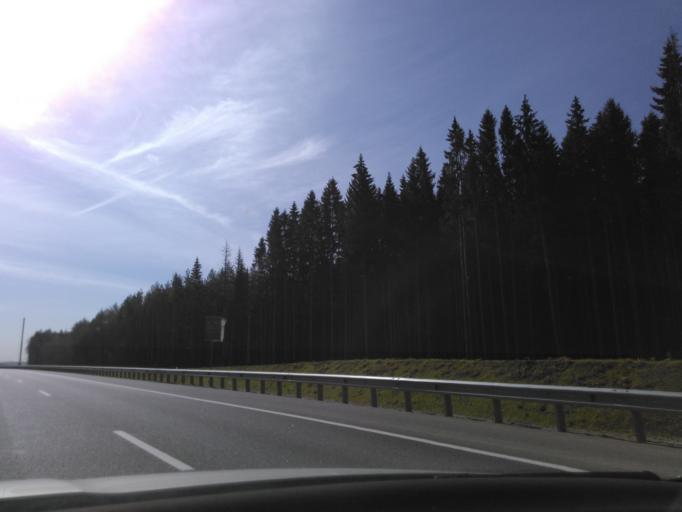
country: RU
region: Moskovskaya
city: Novopodrezkovo
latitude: 55.9687
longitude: 37.3369
